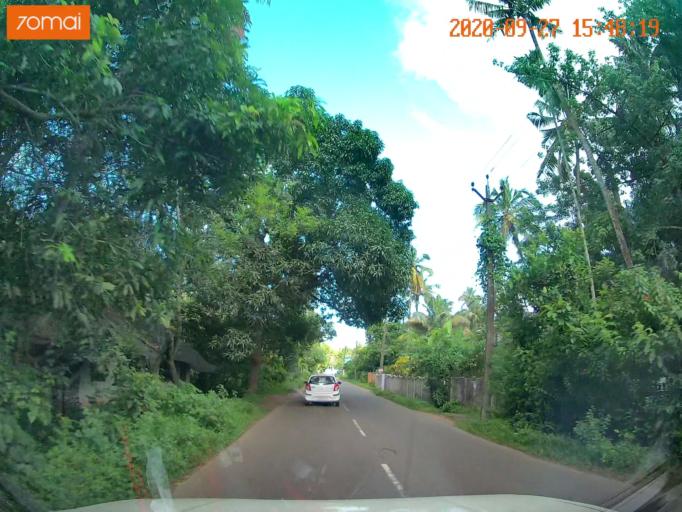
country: IN
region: Kerala
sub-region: Thrissur District
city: Thanniyam
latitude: 10.4830
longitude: 76.1333
